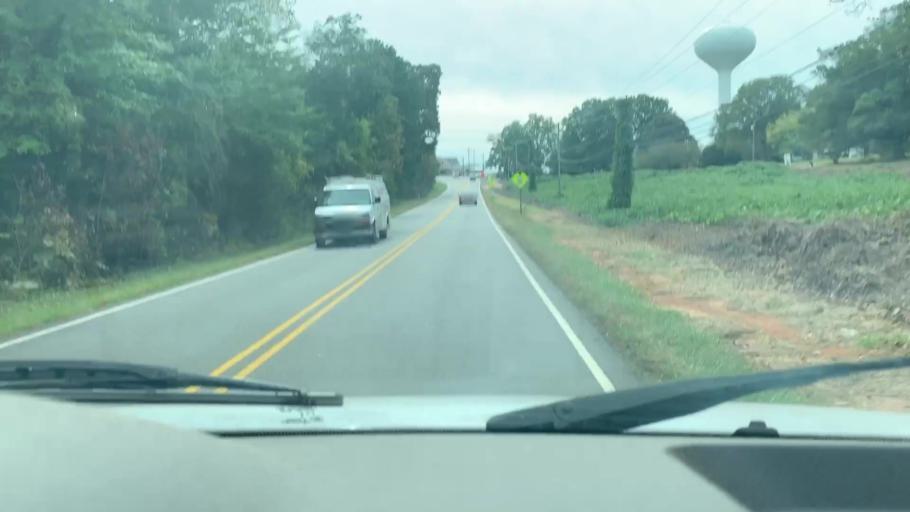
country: US
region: North Carolina
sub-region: Iredell County
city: Mooresville
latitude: 35.5507
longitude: -80.8444
